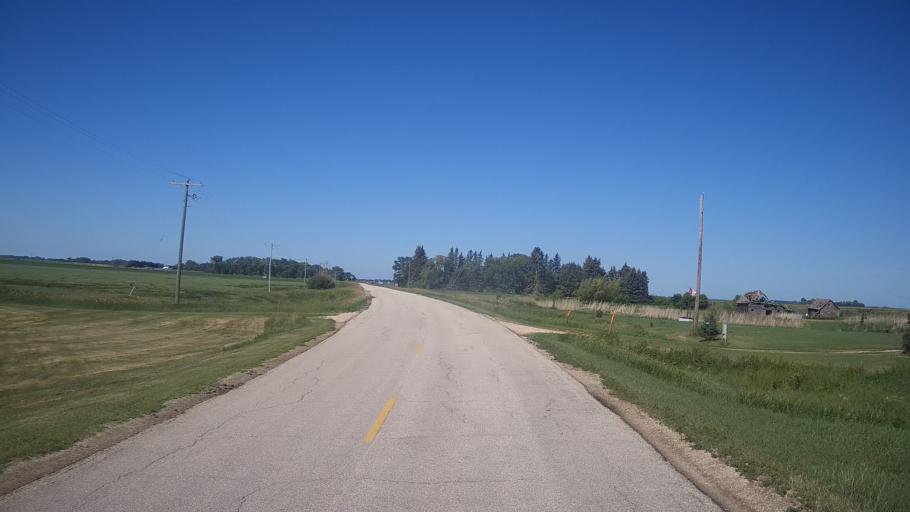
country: CA
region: Manitoba
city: Portage la Prairie
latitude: 50.0436
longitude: -98.0573
